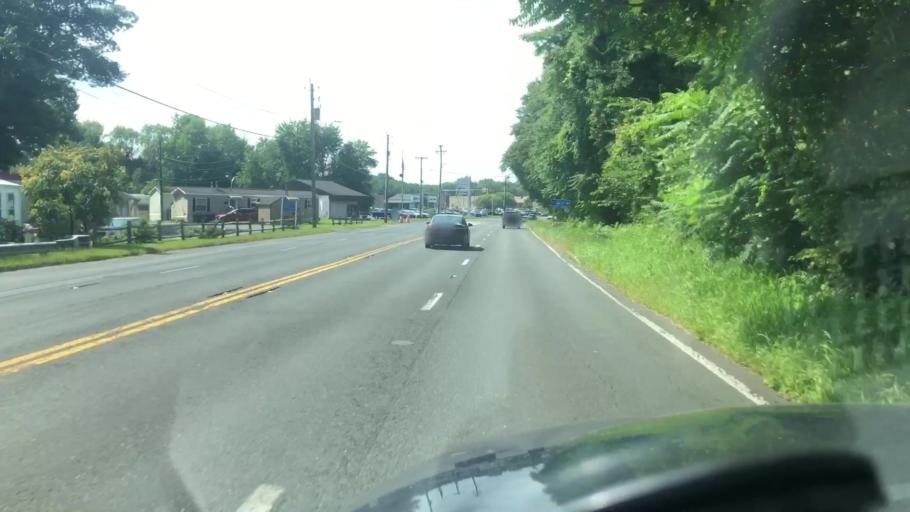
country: US
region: Massachusetts
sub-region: Hampden County
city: Westfield
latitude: 42.1075
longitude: -72.7020
